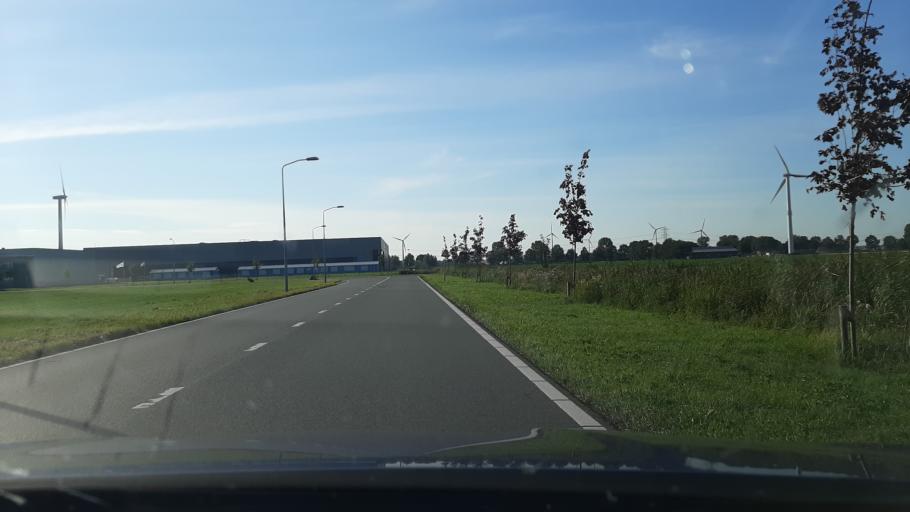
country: NL
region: Flevoland
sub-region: Gemeente Zeewolde
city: Zeewolde
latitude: 52.3648
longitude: 5.5202
